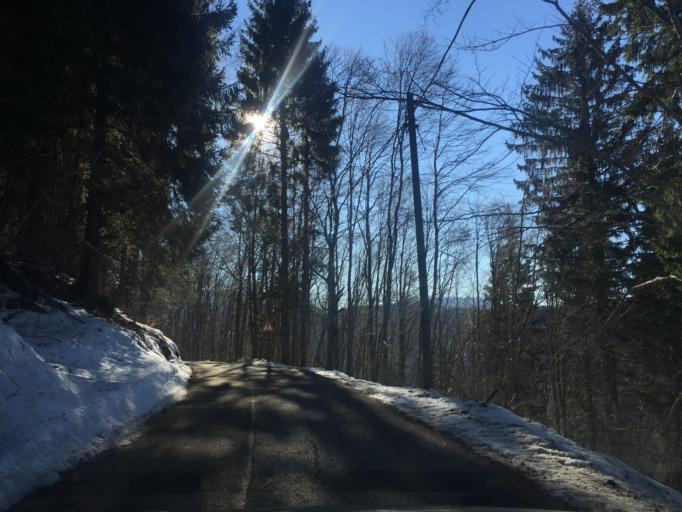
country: IT
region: Friuli Venezia Giulia
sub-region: Provincia di Udine
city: Lauco
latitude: 46.4582
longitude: 12.9280
